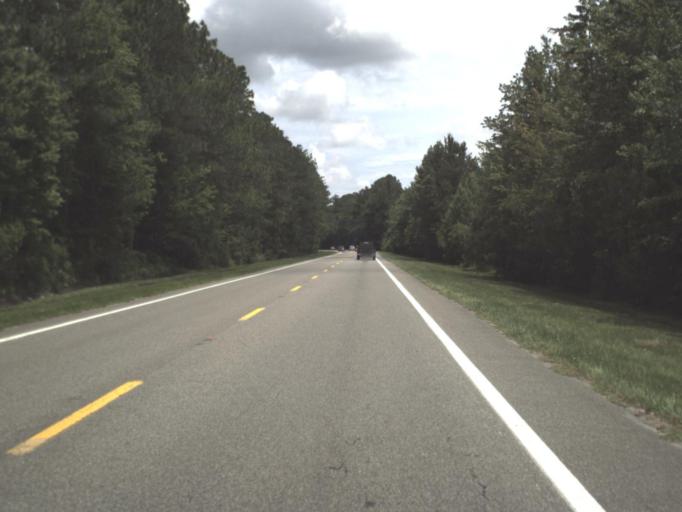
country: US
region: Florida
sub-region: Nassau County
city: Yulee
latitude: 30.6539
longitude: -81.6269
